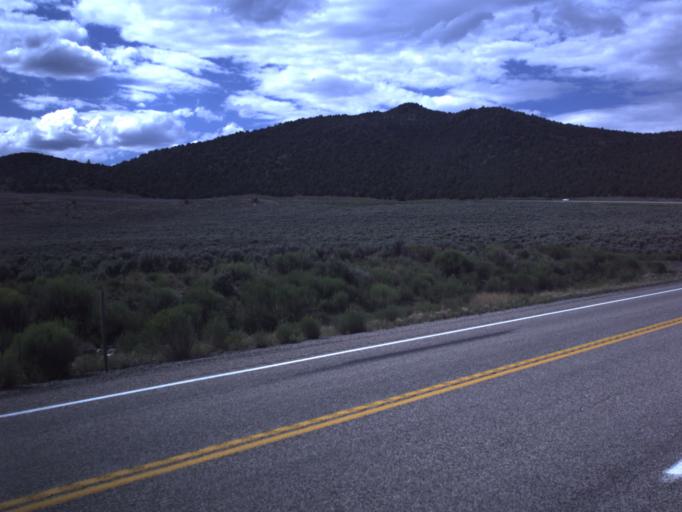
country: US
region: Utah
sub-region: Garfield County
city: Panguitch
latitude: 38.0198
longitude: -112.5097
